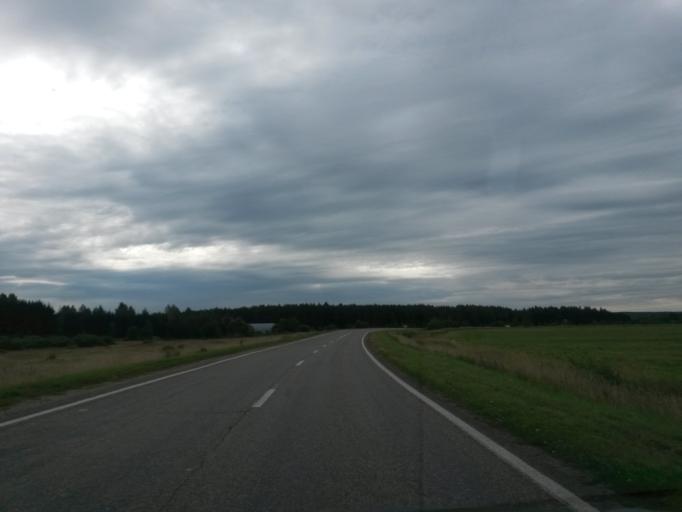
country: RU
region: Jaroslavl
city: Gavrilov-Yam
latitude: 57.3260
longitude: 39.8604
